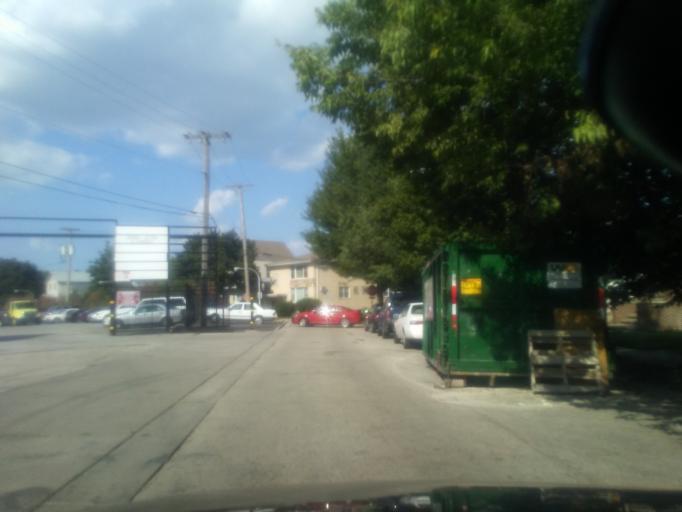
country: US
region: Illinois
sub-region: Cook County
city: Lincolnwood
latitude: 41.9732
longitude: -87.7434
